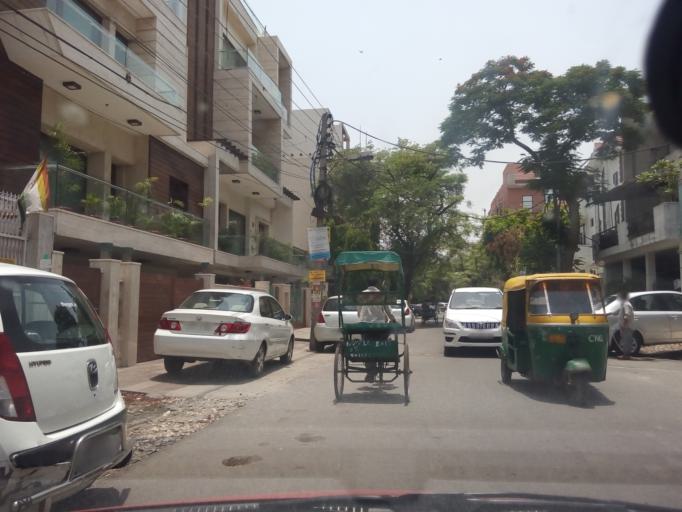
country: IN
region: NCT
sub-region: Central Delhi
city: Karol Bagh
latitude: 28.6930
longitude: 77.1756
